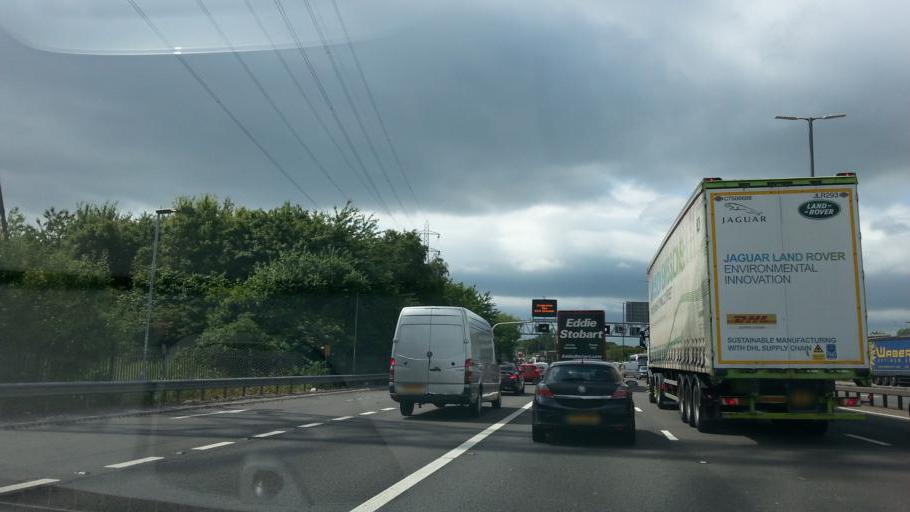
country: GB
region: England
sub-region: City and Borough of Birmingham
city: Hockley
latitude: 52.5249
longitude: -1.8853
